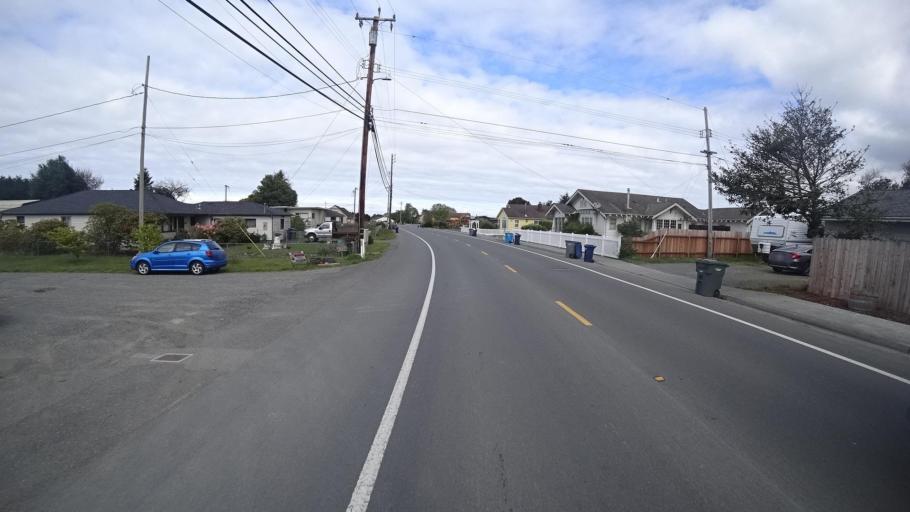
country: US
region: California
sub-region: Humboldt County
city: Arcata
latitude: 40.8924
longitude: -124.0922
